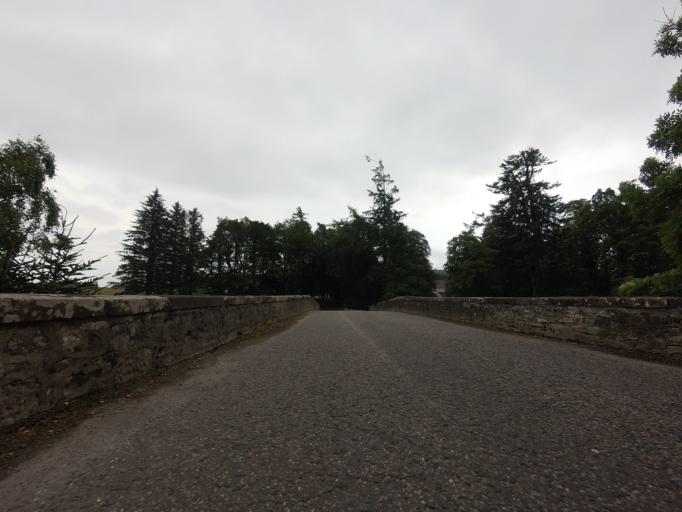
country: GB
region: Scotland
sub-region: Highland
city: Evanton
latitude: 57.8862
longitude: -4.3877
